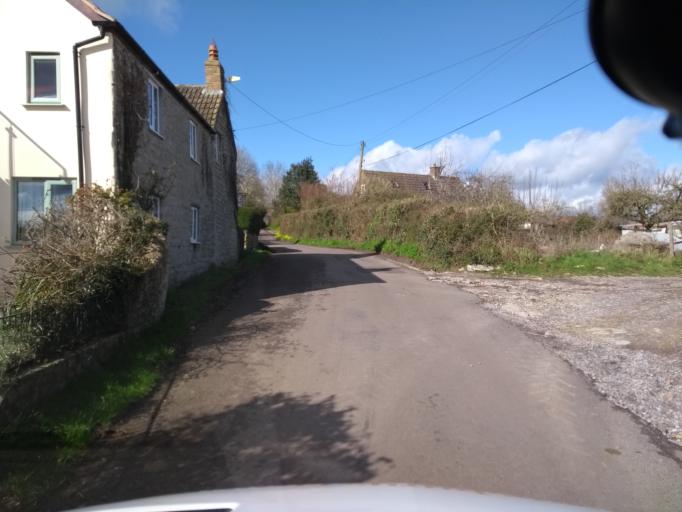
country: GB
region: England
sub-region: Somerset
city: Creech Saint Michael
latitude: 50.9726
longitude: -3.0366
